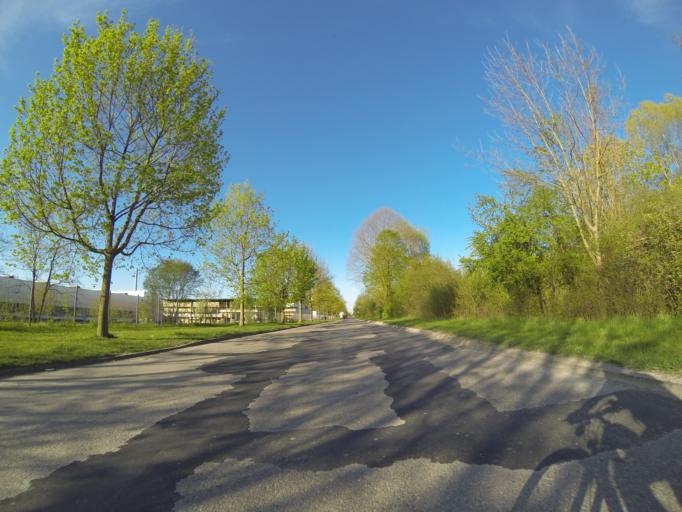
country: DE
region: Baden-Wuerttemberg
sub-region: Tuebingen Region
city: Erbach
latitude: 48.3522
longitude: 9.9424
